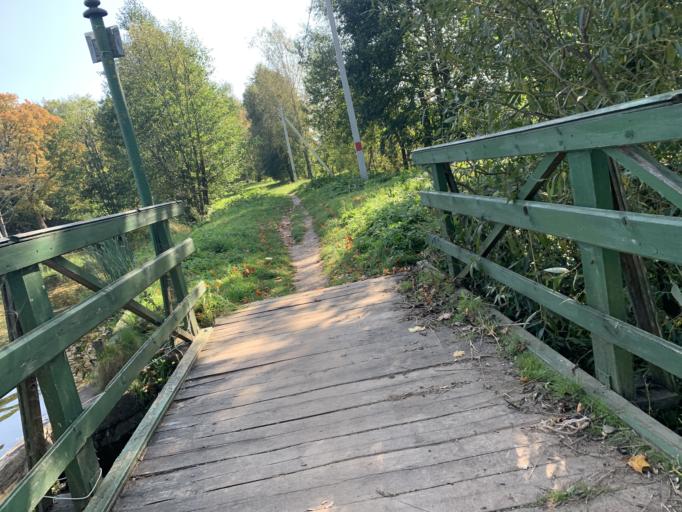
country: BY
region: Minsk
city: Rakaw
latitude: 53.8748
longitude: 26.9708
